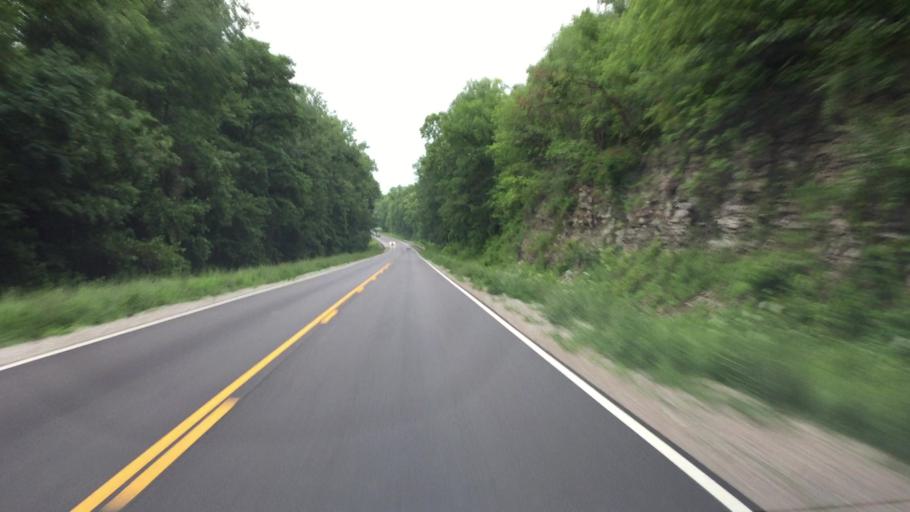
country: US
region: Iowa
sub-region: Lee County
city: Keokuk
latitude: 40.3719
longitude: -91.3979
